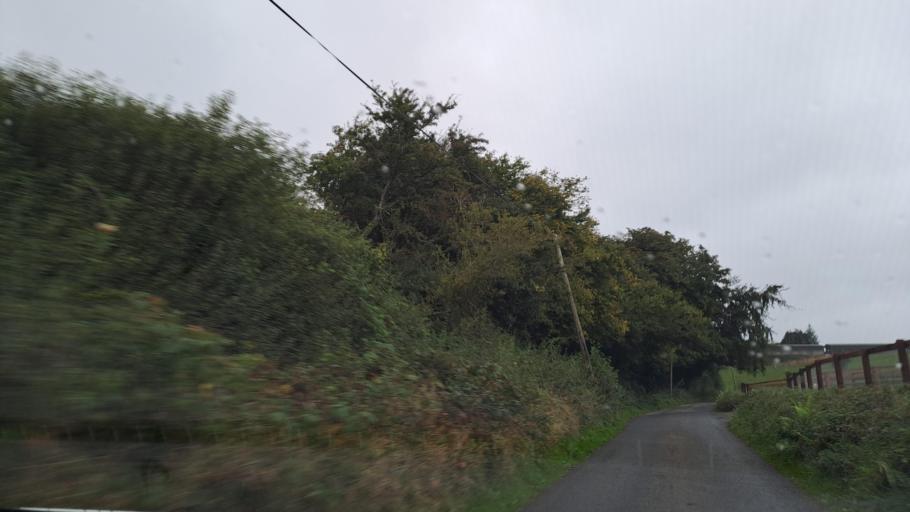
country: IE
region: Ulster
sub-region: An Cabhan
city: Kingscourt
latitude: 54.0007
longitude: -6.8405
